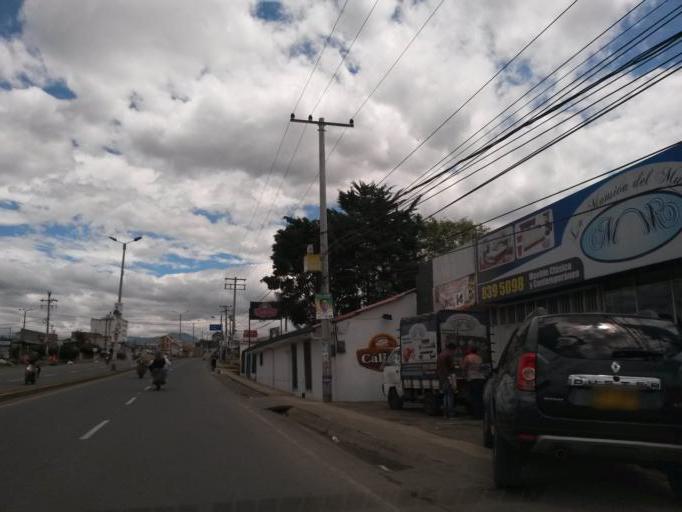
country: CO
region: Cauca
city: Popayan
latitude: 2.4813
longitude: -76.5716
